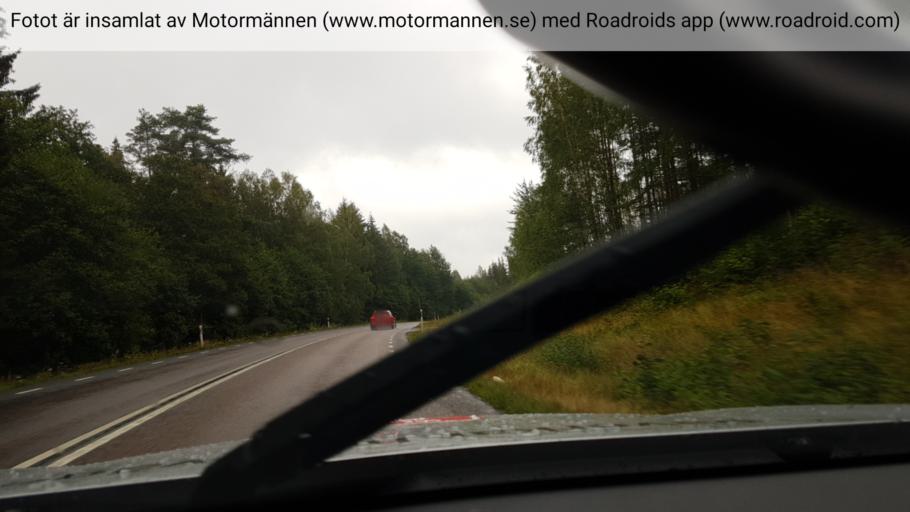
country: SE
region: Vaestra Goetaland
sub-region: Amals Kommun
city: Amal
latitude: 59.0518
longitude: 12.4821
